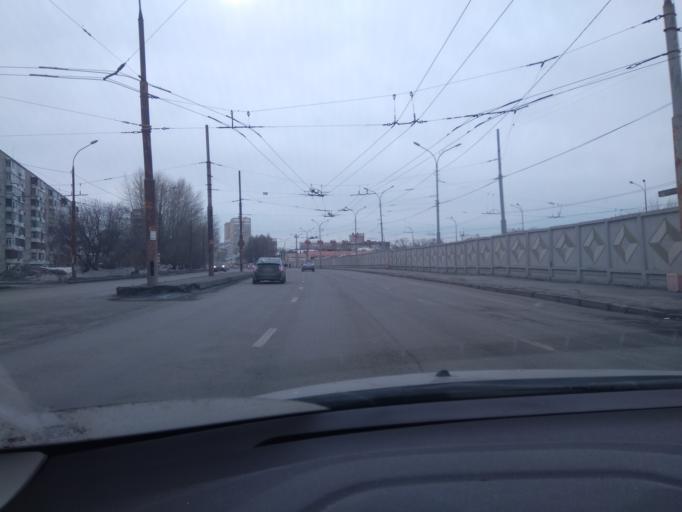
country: RU
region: Sverdlovsk
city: Verkhnyaya Pyshma
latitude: 56.9124
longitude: 60.5974
